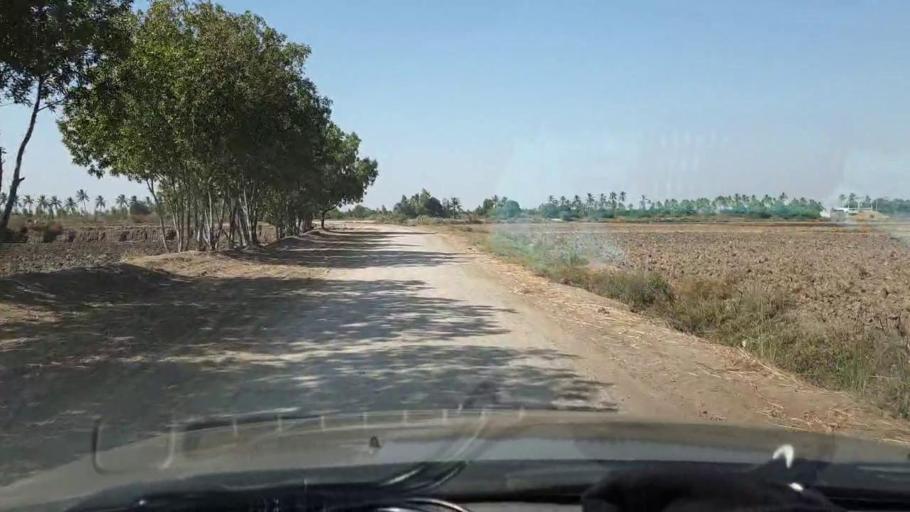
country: PK
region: Sindh
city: Thatta
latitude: 24.6340
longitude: 67.8967
